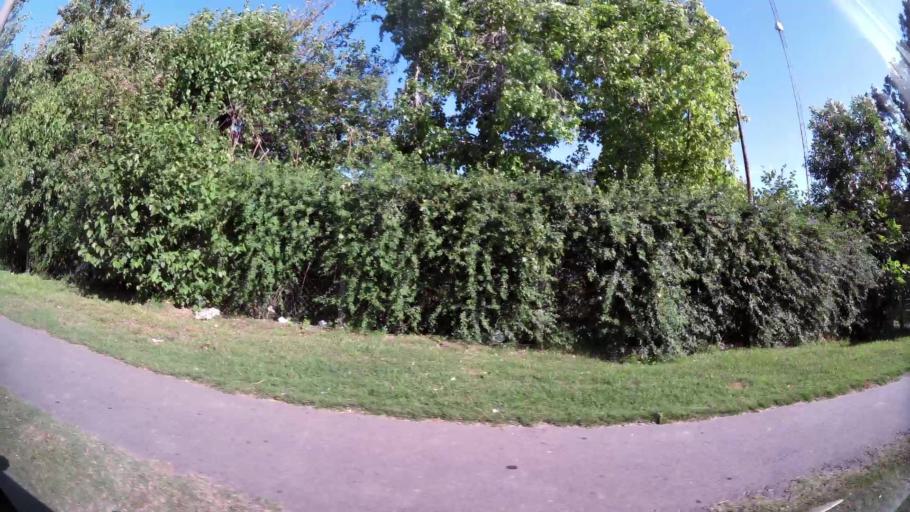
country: AR
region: Buenos Aires
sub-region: Partido de Tigre
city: Tigre
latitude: -34.4770
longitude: -58.6652
